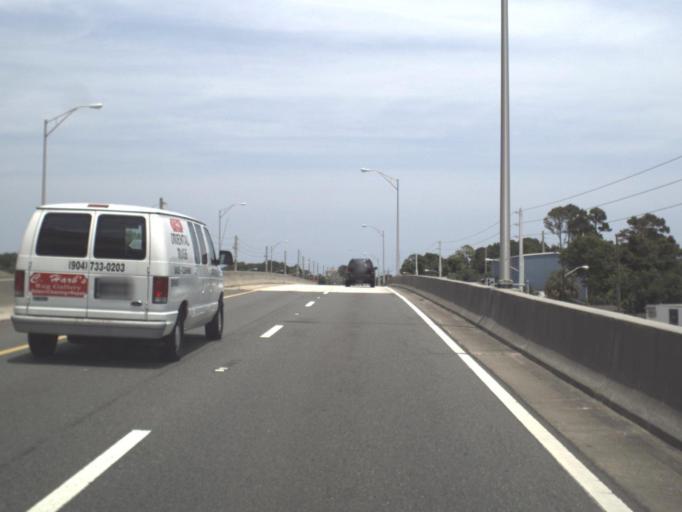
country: US
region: Florida
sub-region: Duval County
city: Atlantic Beach
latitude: 30.3243
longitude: -81.4203
